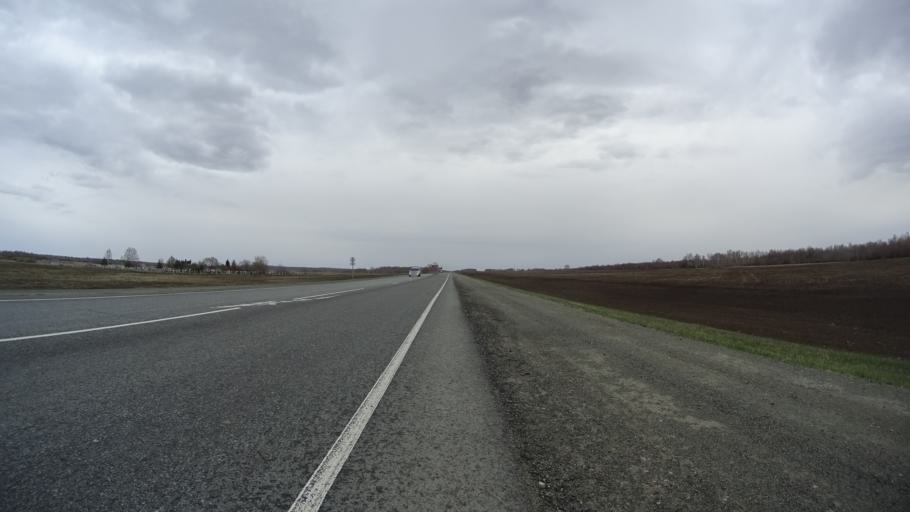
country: RU
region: Chelyabinsk
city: Krasnogorskiy
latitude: 54.6700
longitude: 61.2509
